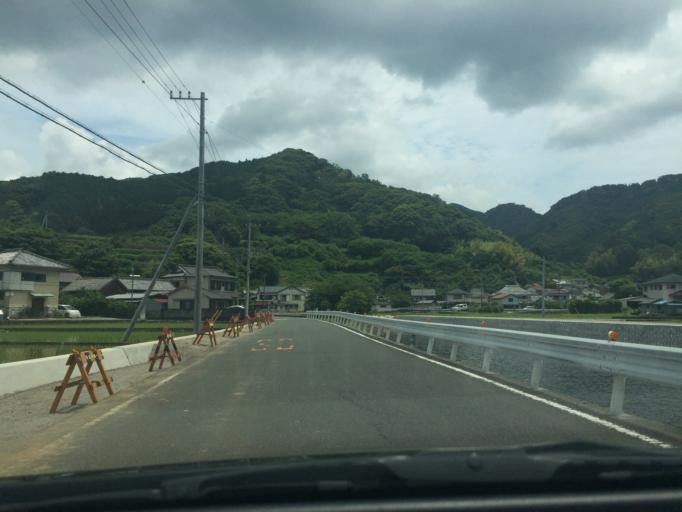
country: JP
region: Shizuoka
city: Shimoda
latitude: 34.7334
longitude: 138.7904
